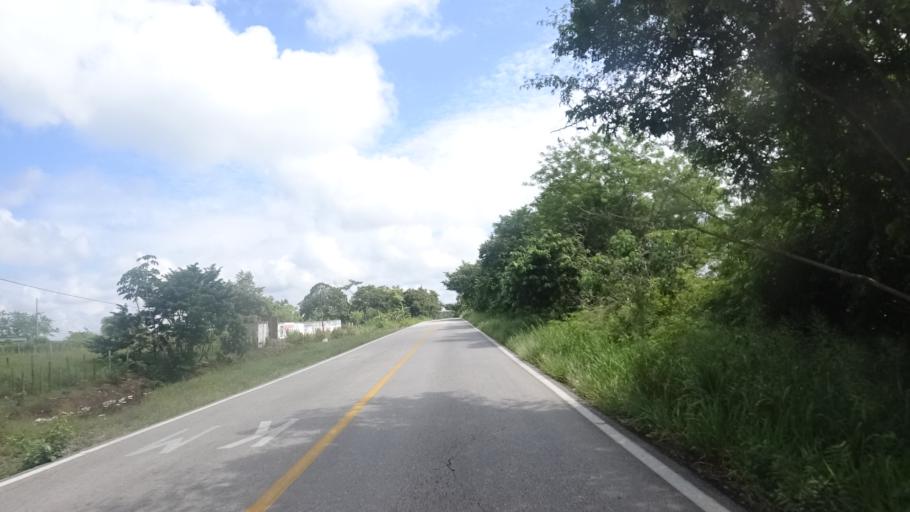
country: MX
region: Chiapas
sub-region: Catazaja
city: Catazaja
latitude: 17.6706
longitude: -92.0324
